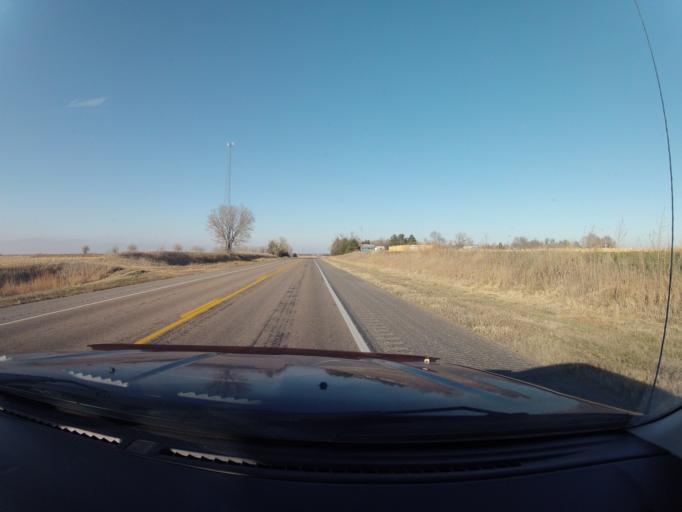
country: US
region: Nebraska
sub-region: Kearney County
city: Minden
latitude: 40.5737
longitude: -98.9519
